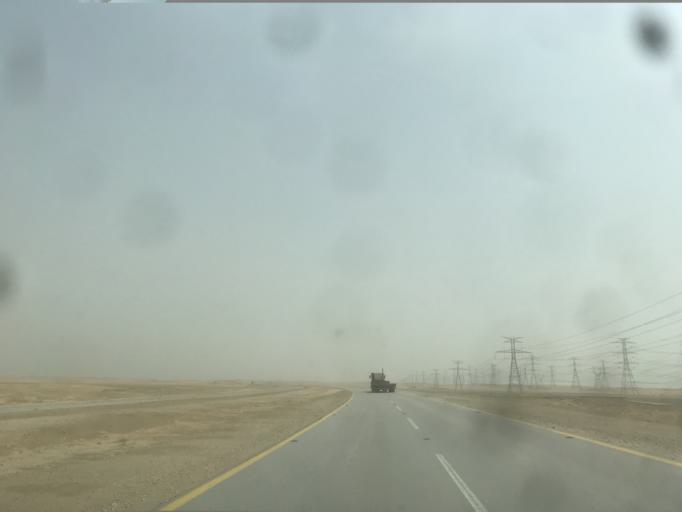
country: SA
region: Eastern Province
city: Abqaiq
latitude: 25.9131
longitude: 49.7988
